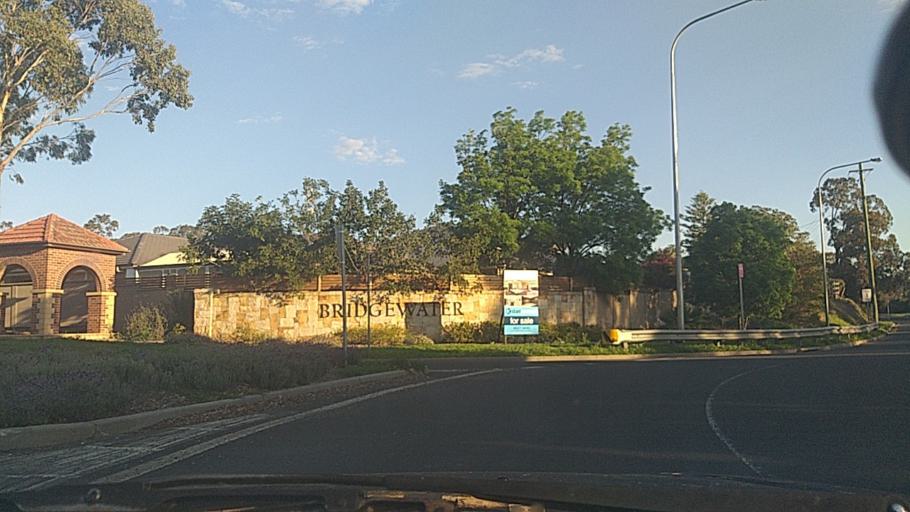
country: AU
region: New South Wales
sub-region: Camden
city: Camden South
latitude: -34.0971
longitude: 150.6953
